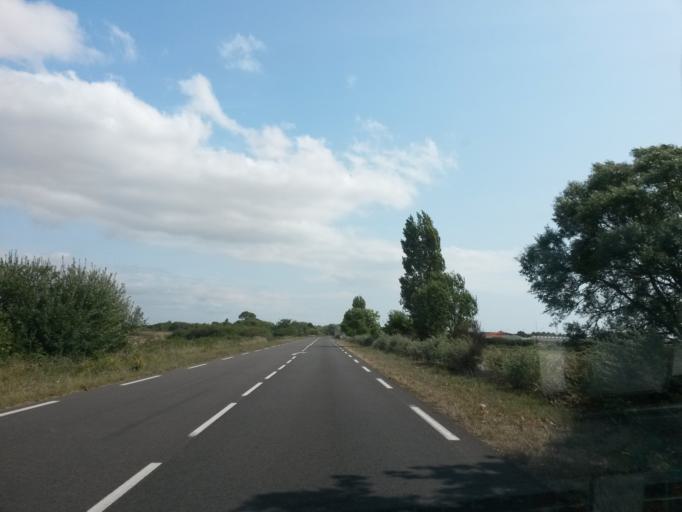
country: FR
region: Pays de la Loire
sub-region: Departement de la Vendee
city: La Tranche-sur-Mer
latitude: 46.3552
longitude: -1.4379
